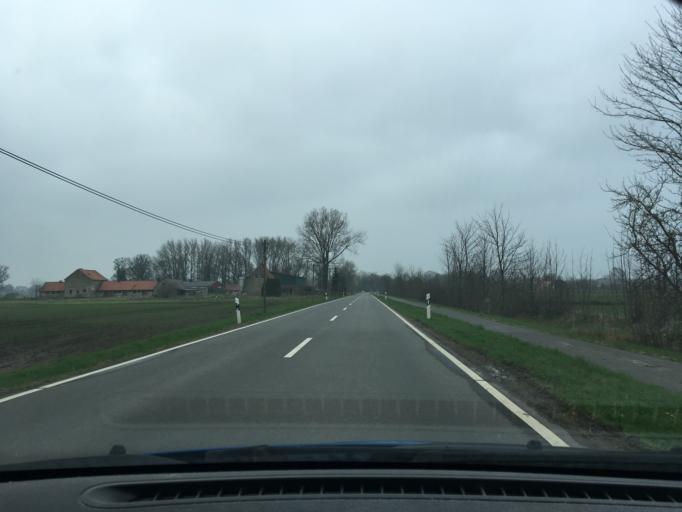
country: DE
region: Lower Saxony
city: Neu Darchau
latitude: 53.2969
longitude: 10.8860
